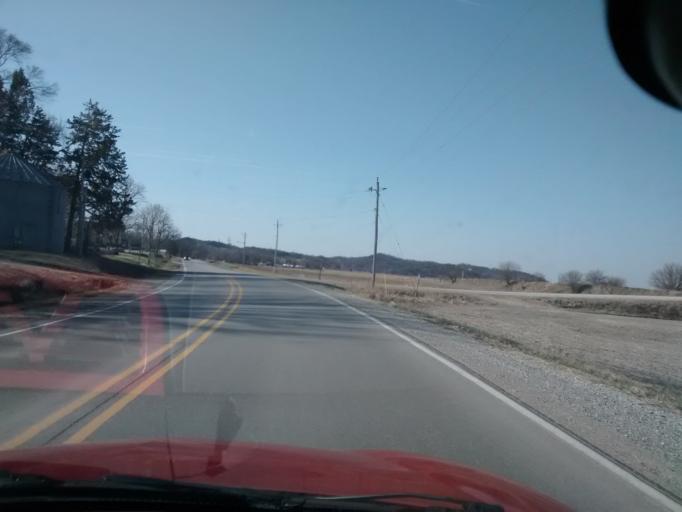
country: US
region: Iowa
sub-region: Pottawattamie County
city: Carter Lake
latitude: 41.3771
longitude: -95.8564
